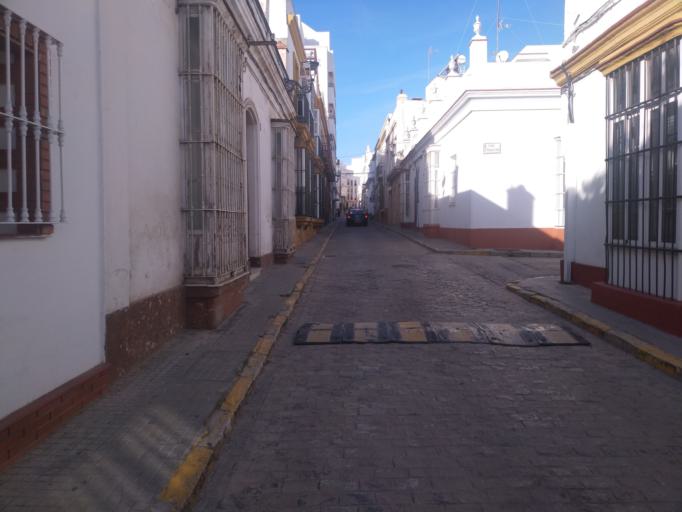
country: ES
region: Andalusia
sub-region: Provincia de Cadiz
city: San Fernando
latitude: 36.4701
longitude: -6.1948
